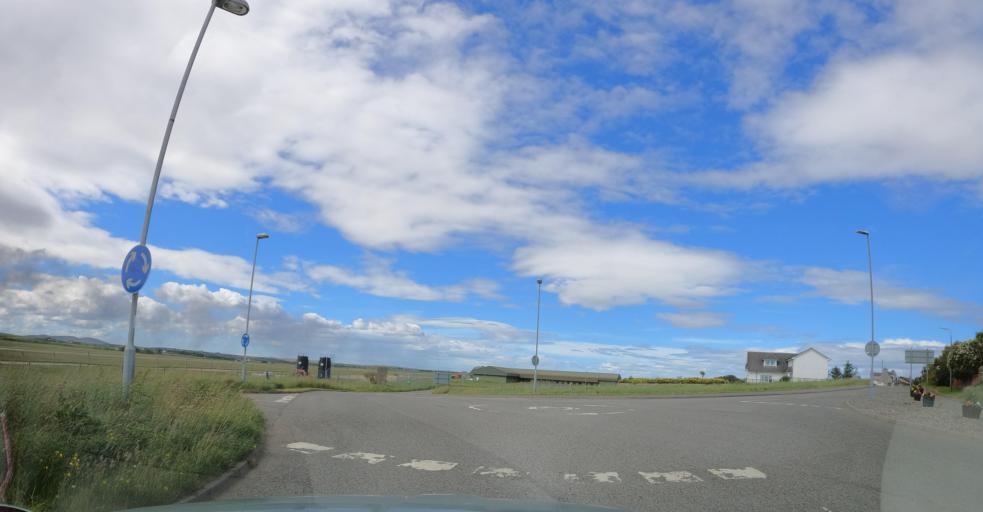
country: GB
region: Scotland
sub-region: Eilean Siar
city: Stornoway
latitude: 58.2095
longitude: -6.3231
